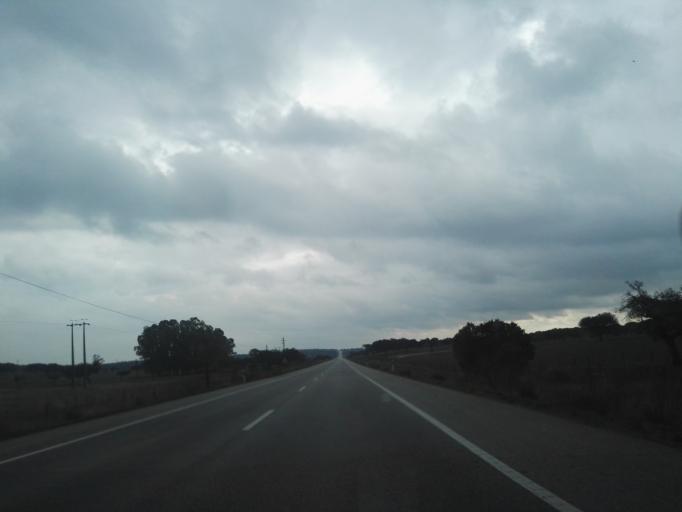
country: PT
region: Portalegre
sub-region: Arronches
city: Arronches
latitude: 39.1703
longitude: -7.3321
